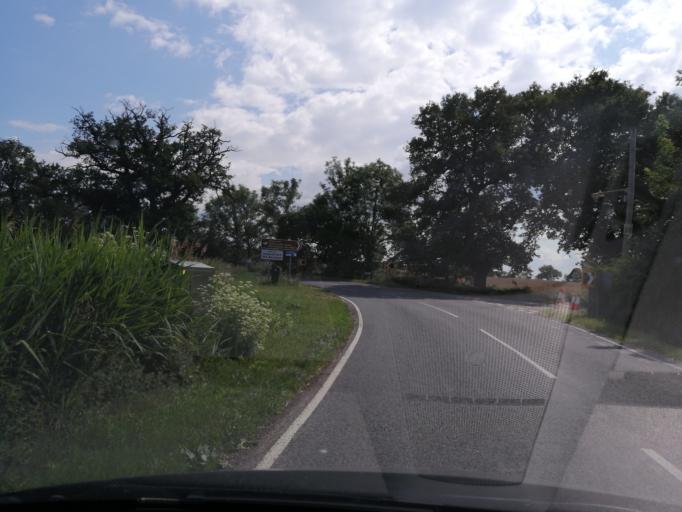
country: GB
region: England
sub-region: Cambridgeshire
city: Ramsey
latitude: 52.4466
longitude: -0.1599
